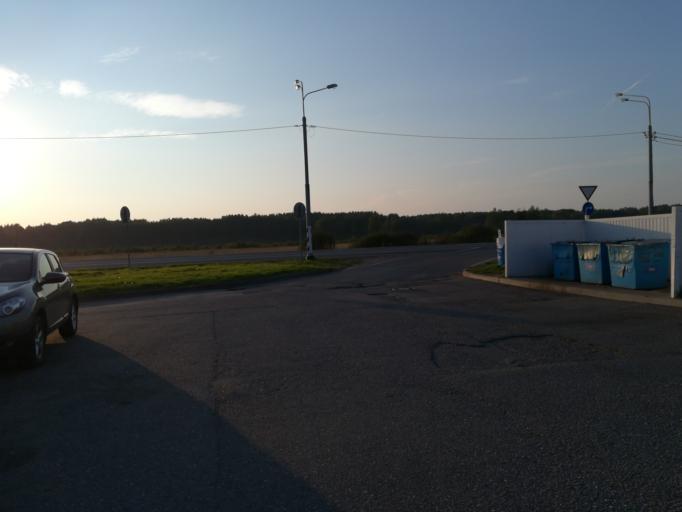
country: RU
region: Novgorod
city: Chudovo
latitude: 58.9078
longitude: 31.5040
